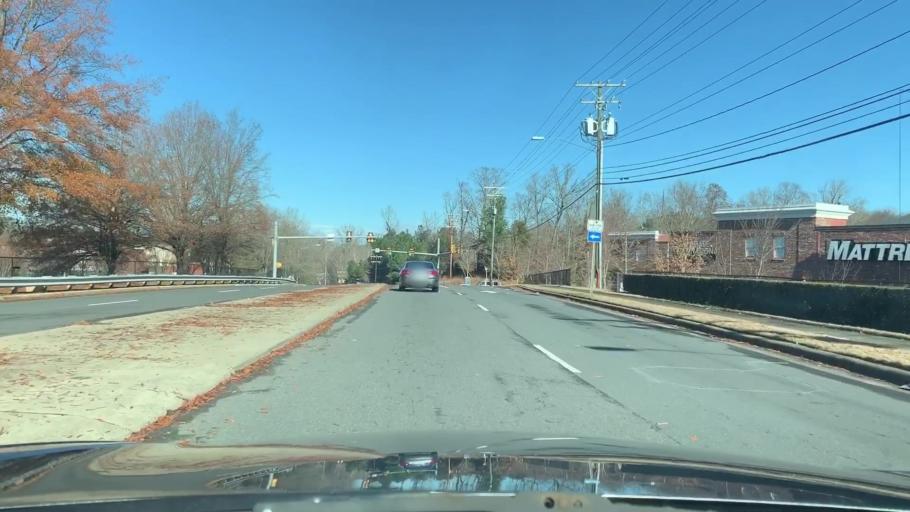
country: US
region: North Carolina
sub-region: Orange County
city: Chapel Hill
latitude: 35.9547
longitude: -78.9944
